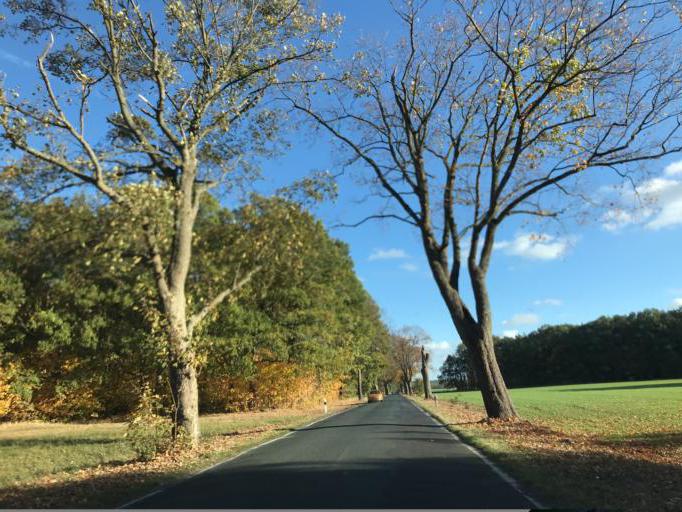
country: DE
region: Brandenburg
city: Sonnenberg
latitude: 53.0115
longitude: 13.0984
